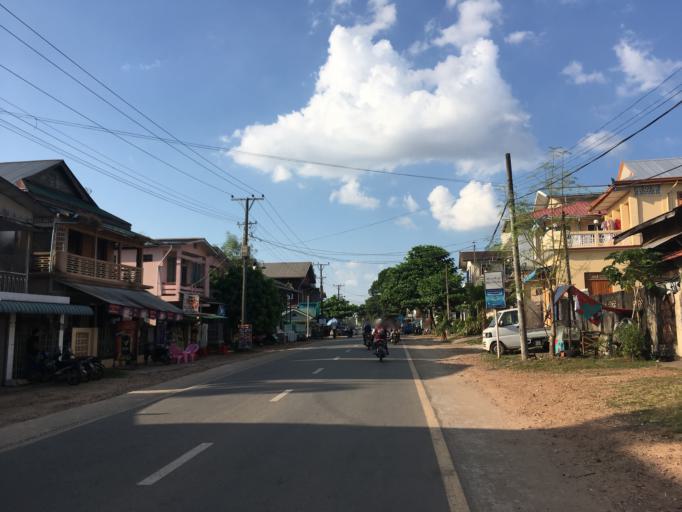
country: MM
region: Mon
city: Mawlamyine
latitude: 16.4583
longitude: 97.6262
